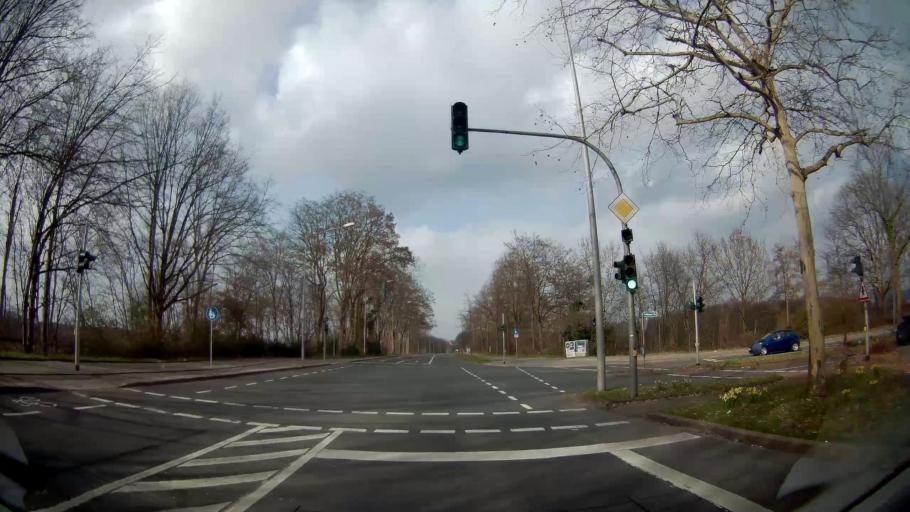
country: DE
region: North Rhine-Westphalia
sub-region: Regierungsbezirk Munster
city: Gladbeck
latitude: 51.5817
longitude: 6.9888
